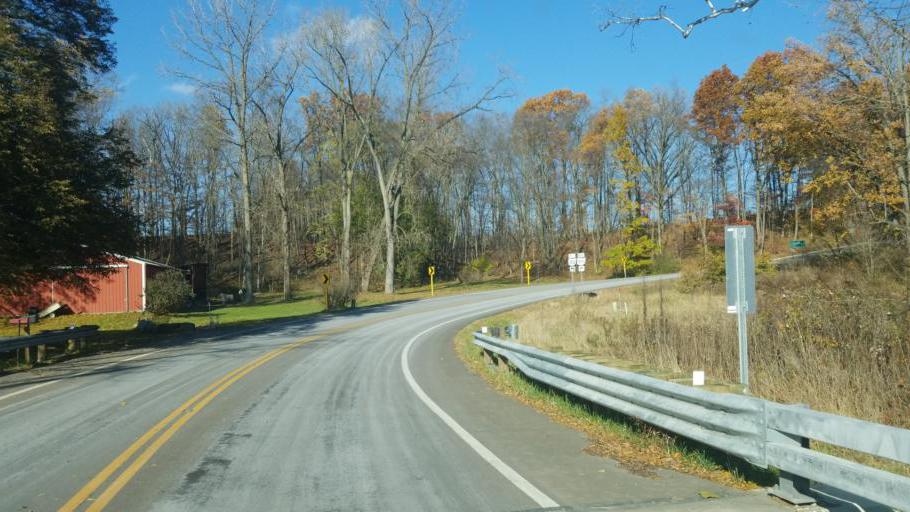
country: US
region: Ohio
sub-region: Ashland County
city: Ashland
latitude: 40.9357
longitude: -82.3152
